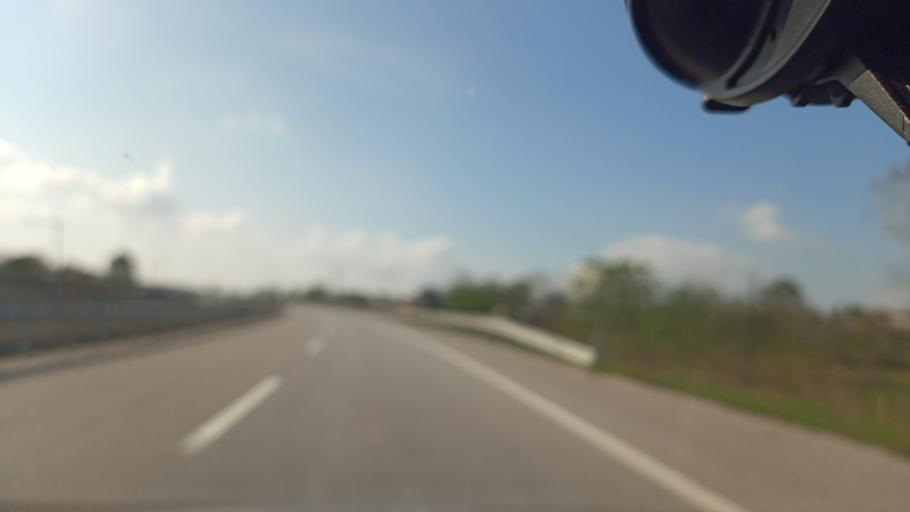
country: TR
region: Sakarya
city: Kaynarca
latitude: 41.0341
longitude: 30.3290
